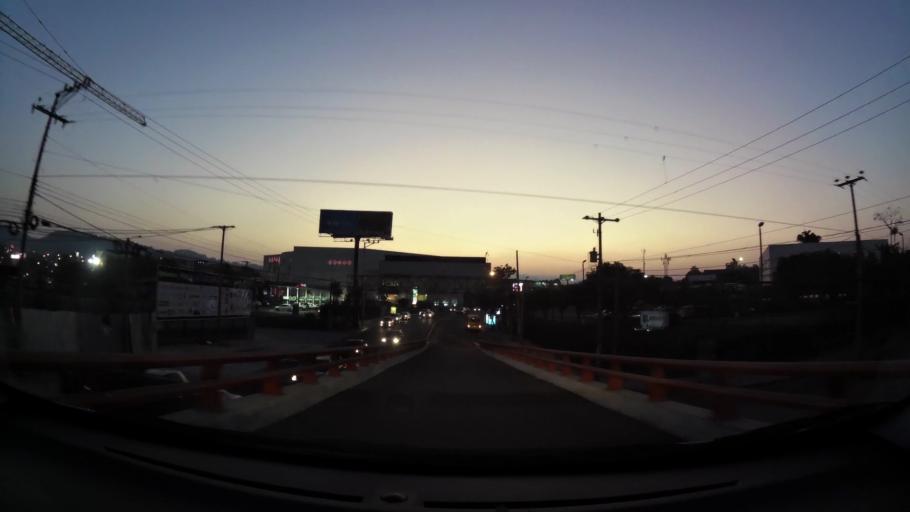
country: SV
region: La Libertad
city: Antiguo Cuscatlan
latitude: 13.6790
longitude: -89.2523
